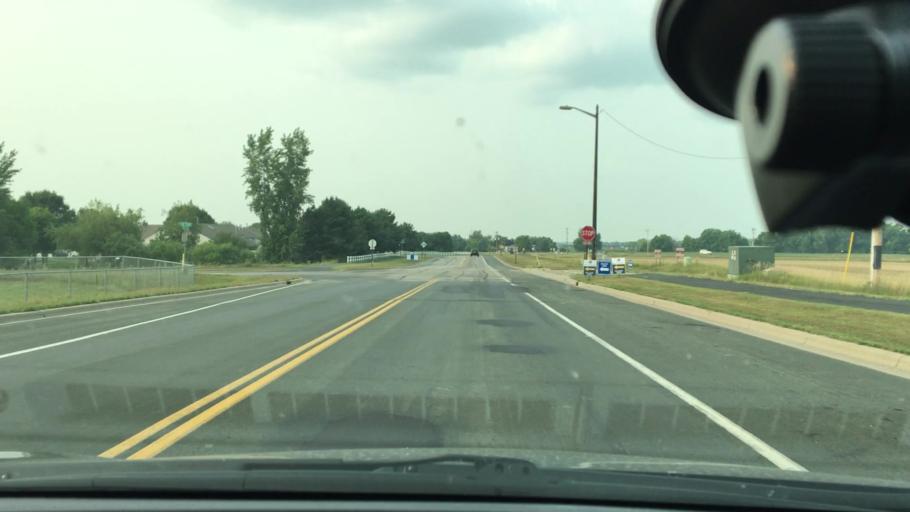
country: US
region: Minnesota
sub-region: Wright County
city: Otsego
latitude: 45.2627
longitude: -93.5605
